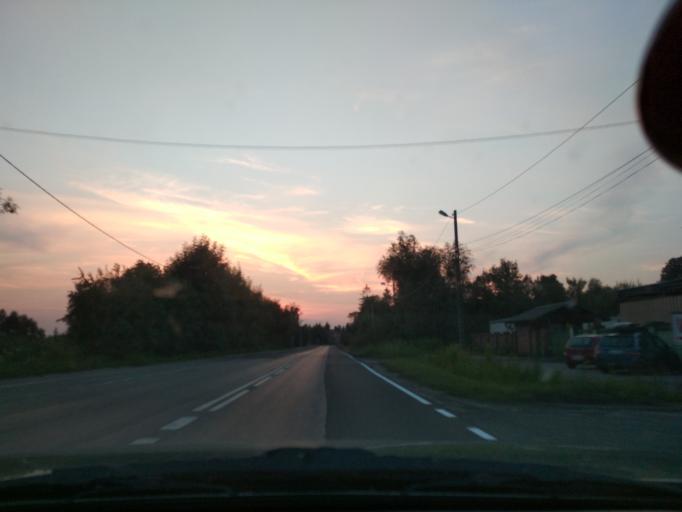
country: PL
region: Silesian Voivodeship
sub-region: Powiat zawiercianski
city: Ogrodzieniec
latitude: 50.4552
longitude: 19.5047
